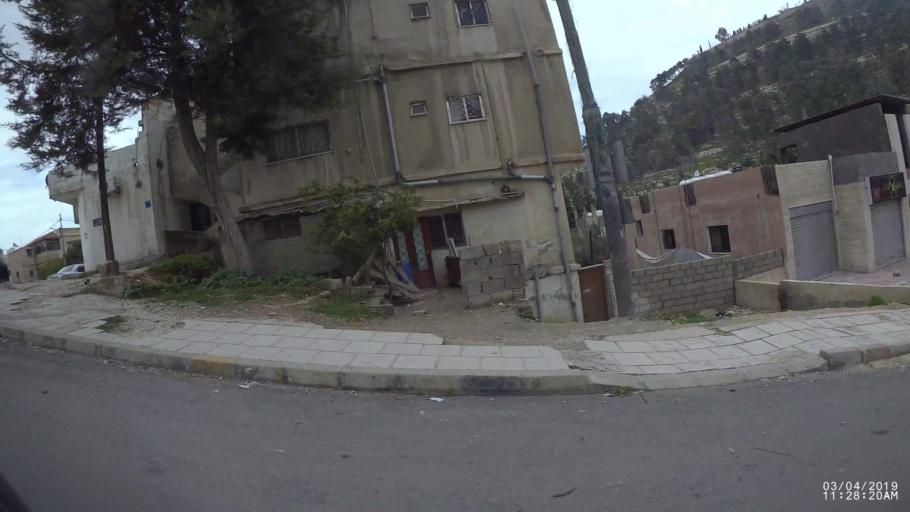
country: JO
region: Amman
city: Wadi as Sir
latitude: 31.9554
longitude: 35.8213
